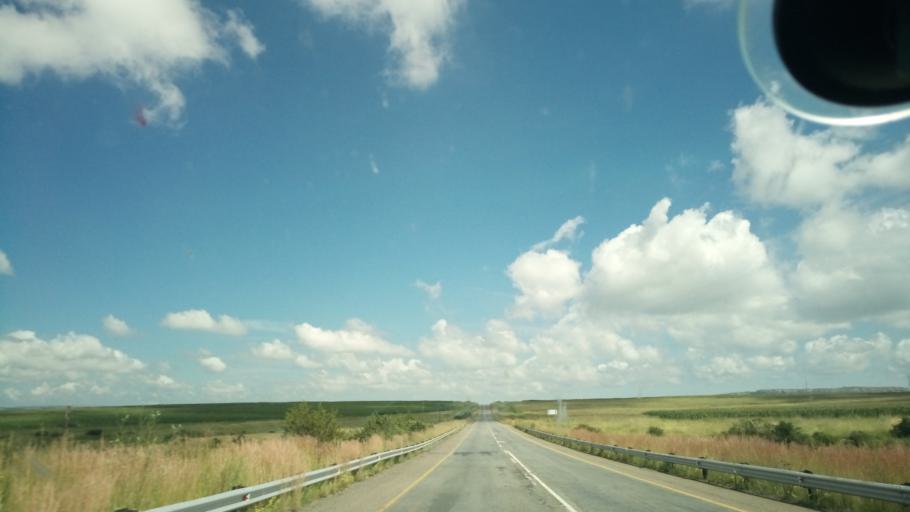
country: ZA
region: Orange Free State
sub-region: Thabo Mofutsanyana District Municipality
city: Ficksburg
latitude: -28.9017
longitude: 27.7920
